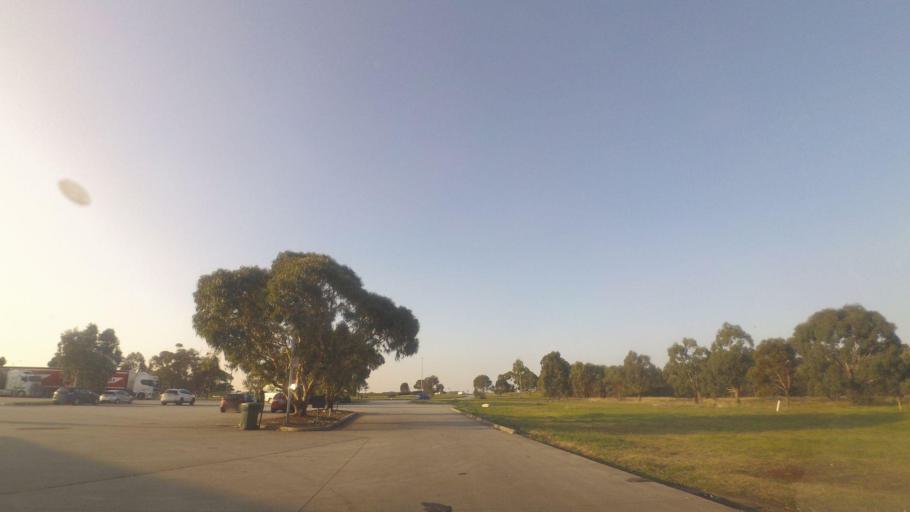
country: AU
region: Victoria
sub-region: Wyndham
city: Werribee
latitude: -37.9275
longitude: 144.6318
